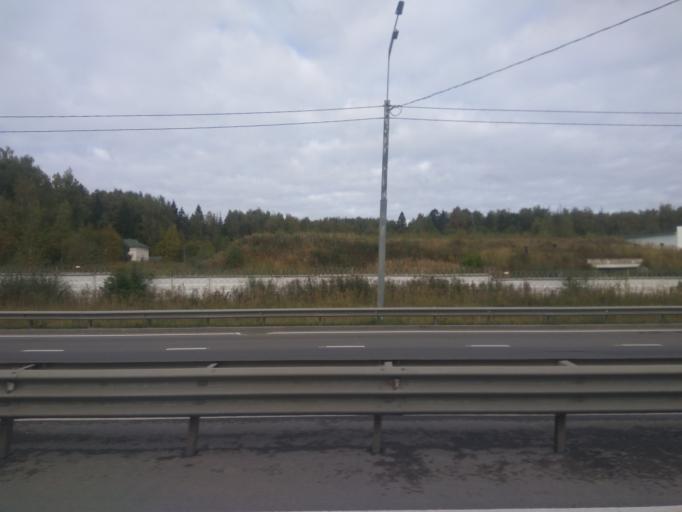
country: RU
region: Moskovskaya
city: Fryazino
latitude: 55.9397
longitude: 38.0329
